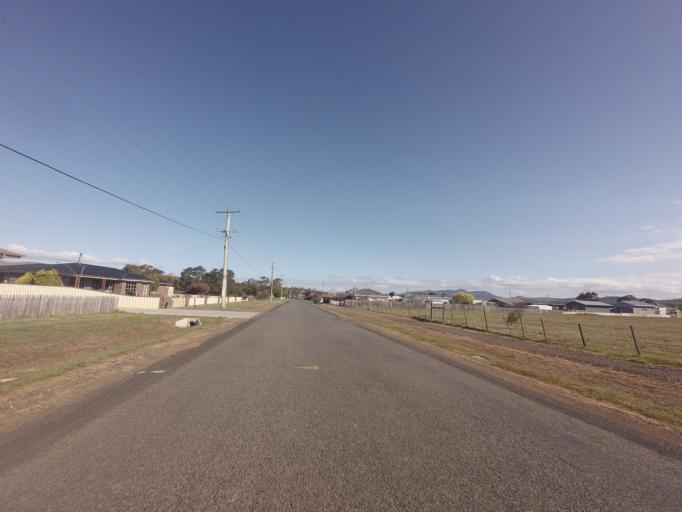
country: AU
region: Tasmania
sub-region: Sorell
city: Sorell
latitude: -42.5046
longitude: 147.9158
